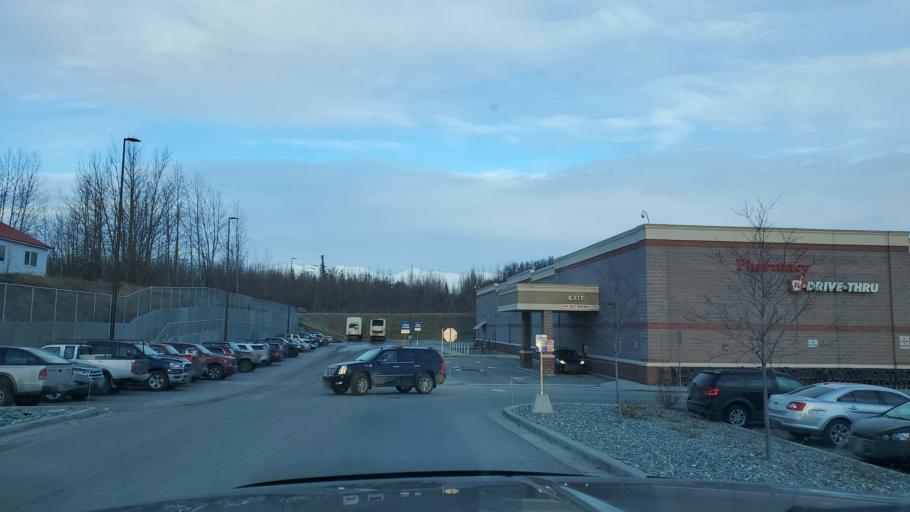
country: US
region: Alaska
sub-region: Matanuska-Susitna Borough
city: Palmer
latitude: 61.6000
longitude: -149.1270
